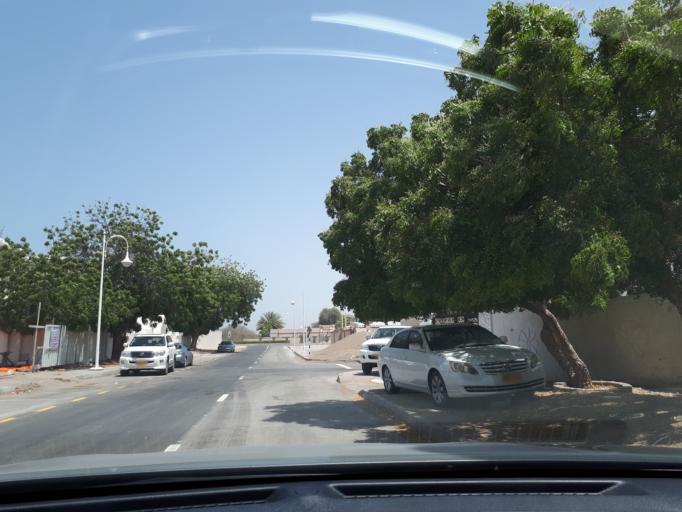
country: OM
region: Muhafazat Masqat
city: As Sib al Jadidah
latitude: 23.7114
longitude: 58.0749
